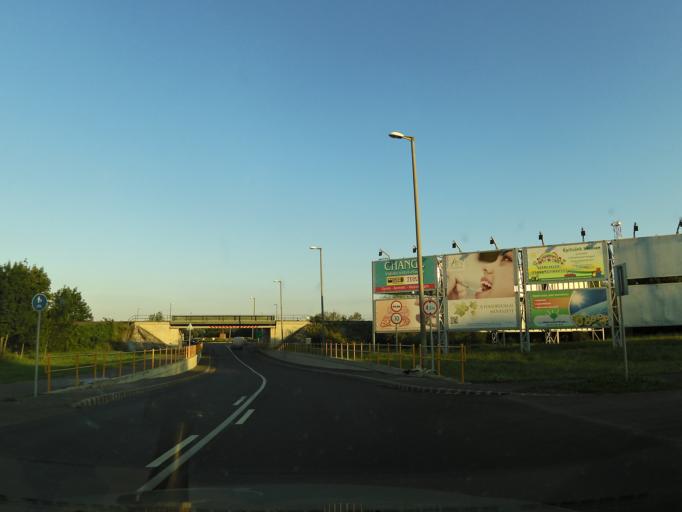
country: HU
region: Csongrad
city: Hodmezovasarhely
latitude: 46.4080
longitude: 20.3226
